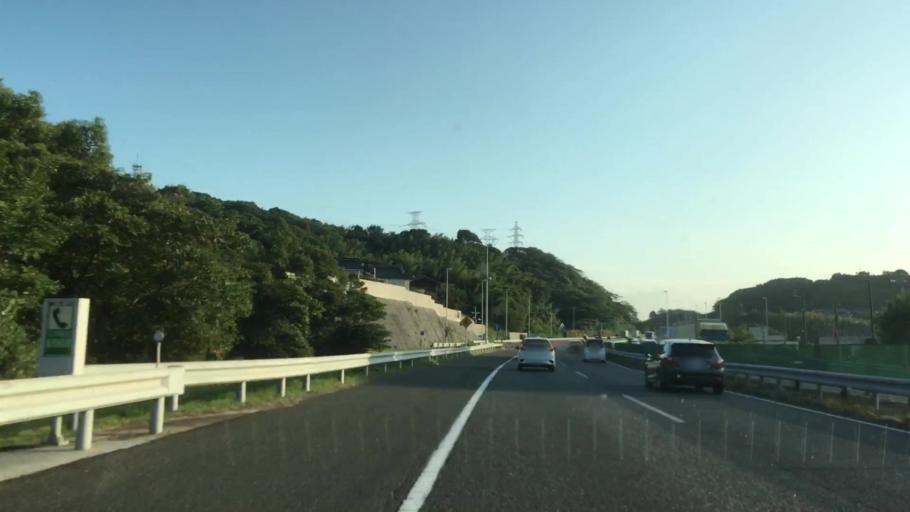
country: JP
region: Yamaguchi
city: Shimonoseki
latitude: 33.9777
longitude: 130.9524
